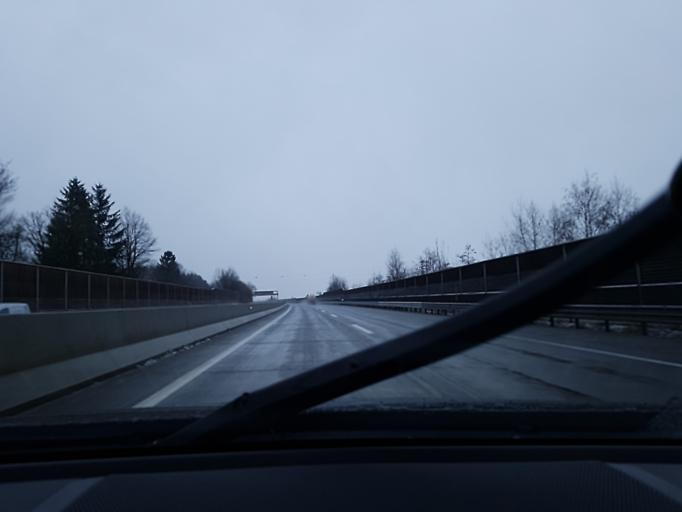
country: AT
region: Salzburg
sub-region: Politischer Bezirk Hallein
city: Golling an der Salzach
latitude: 47.6017
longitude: 13.1497
